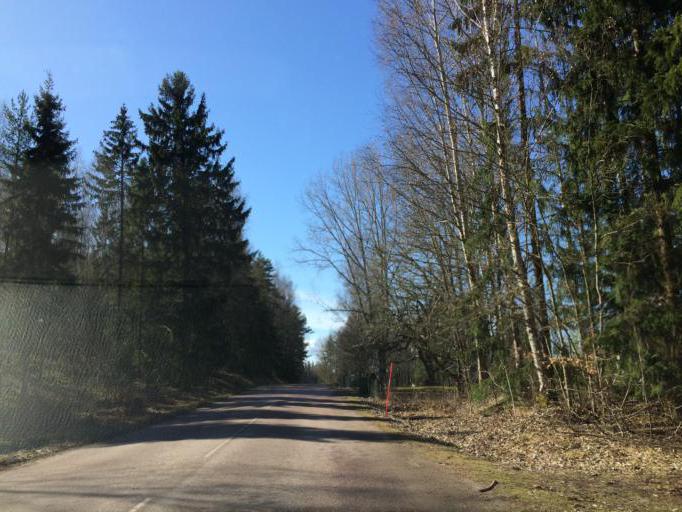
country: SE
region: Soedermanland
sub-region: Eskilstuna Kommun
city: Kvicksund
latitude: 59.5087
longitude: 16.2866
